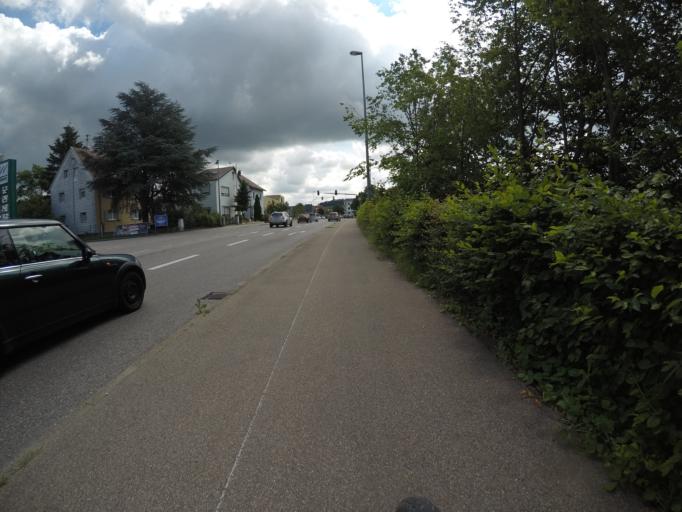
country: DE
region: Baden-Wuerttemberg
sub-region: Regierungsbezirk Stuttgart
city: Uhingen
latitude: 48.7089
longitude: 9.5771
